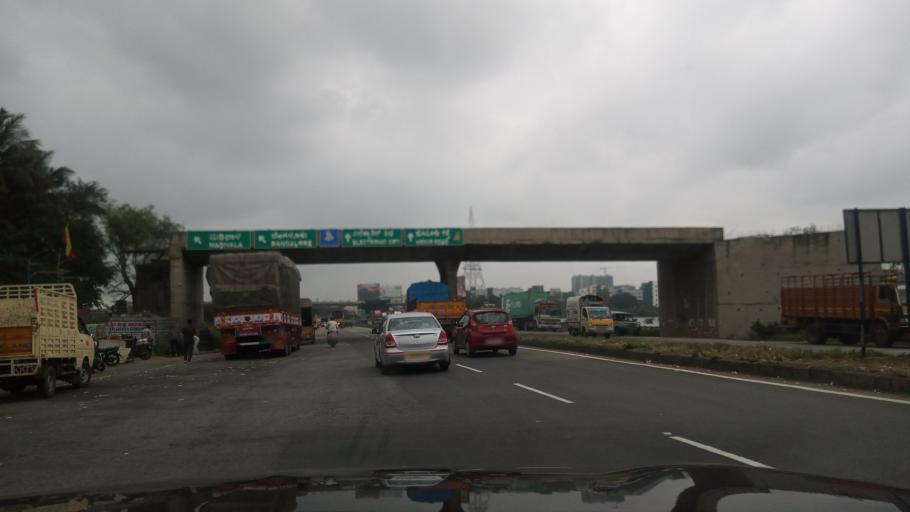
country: IN
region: Karnataka
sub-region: Bangalore Urban
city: Bangalore
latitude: 12.8584
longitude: 77.6580
